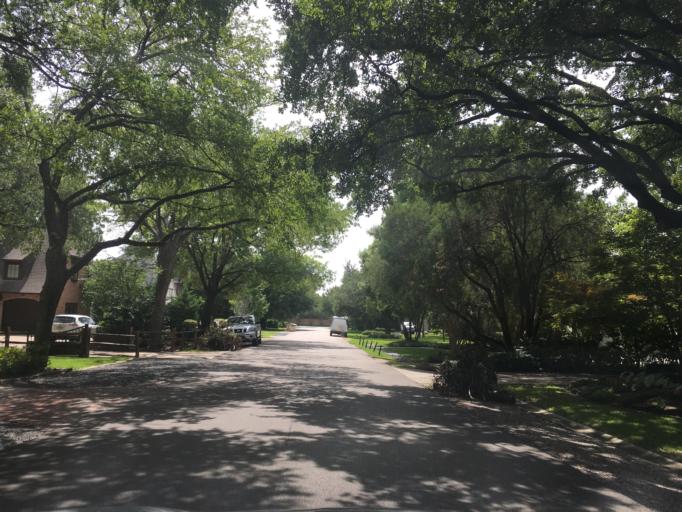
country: US
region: Texas
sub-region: Dallas County
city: University Park
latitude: 32.8874
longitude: -96.8020
